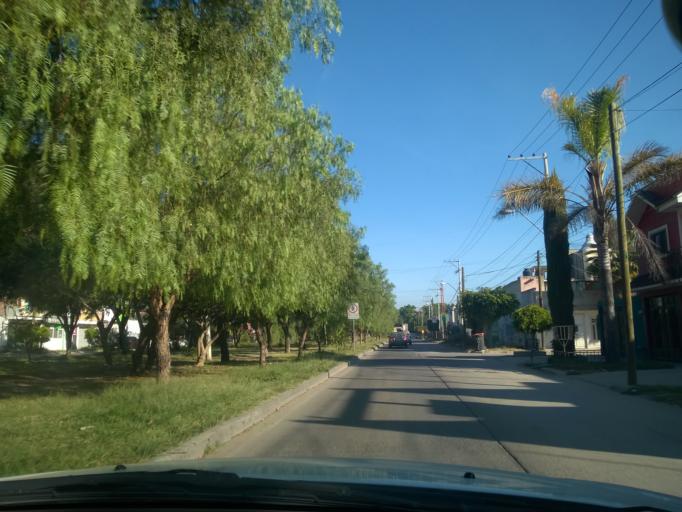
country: MX
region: Guanajuato
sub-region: Leon
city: San Jose de Duran (Los Troncoso)
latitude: 21.0734
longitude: -101.6453
